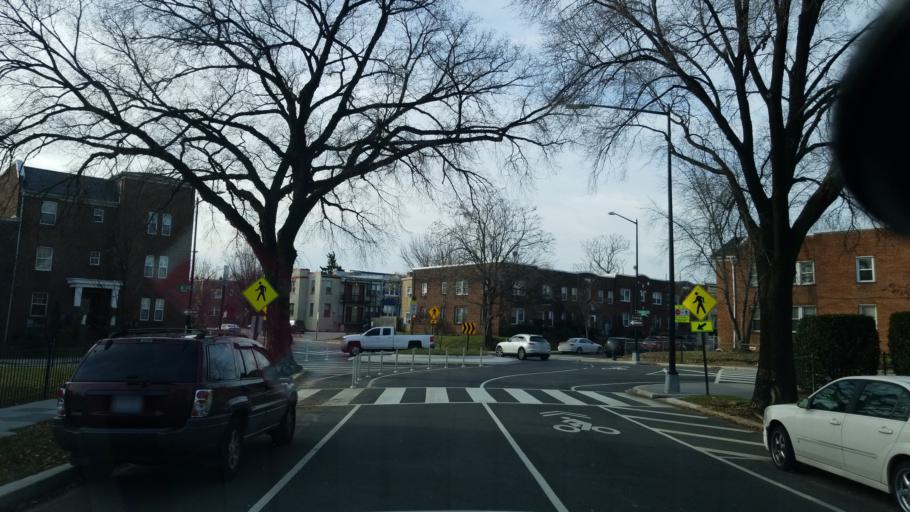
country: US
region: Maryland
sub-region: Prince George's County
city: Mount Rainier
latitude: 38.8965
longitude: -76.9804
